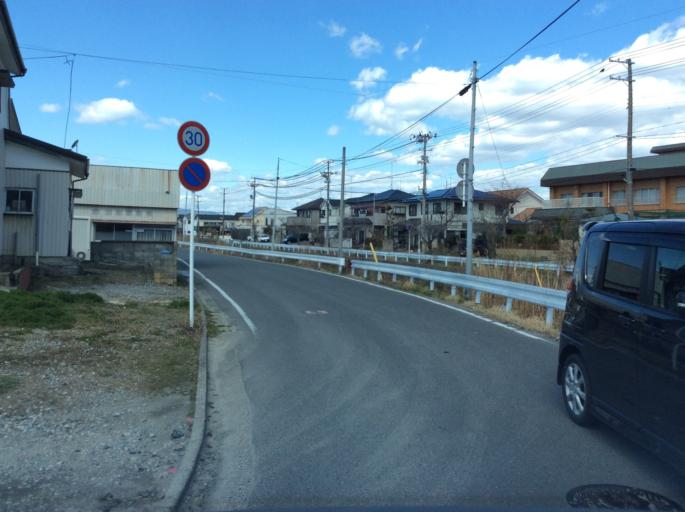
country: JP
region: Fukushima
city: Iwaki
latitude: 36.9504
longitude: 140.9102
